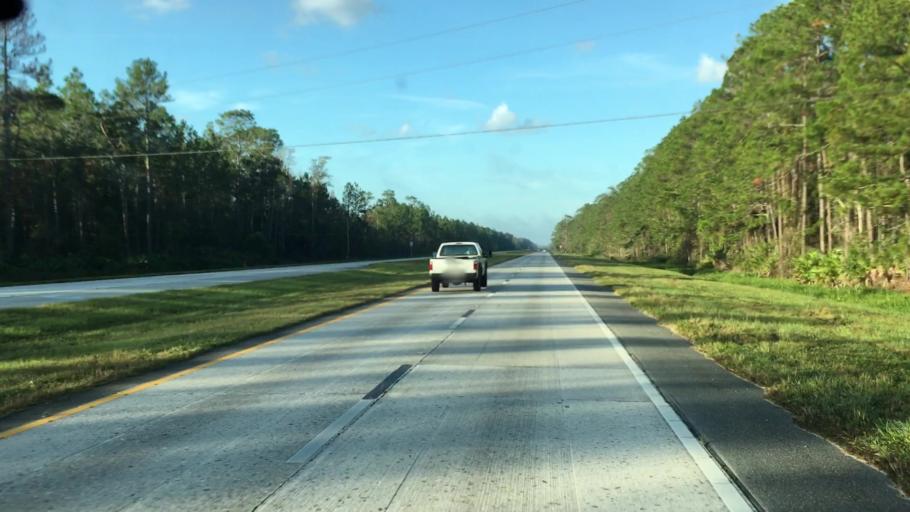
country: US
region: Florida
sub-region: Volusia County
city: Samsula-Spruce Creek
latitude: 29.1195
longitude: -81.1790
